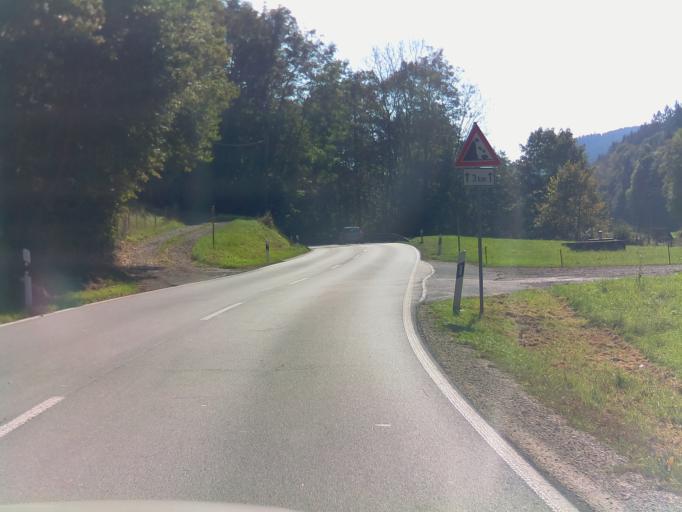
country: DE
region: Thuringia
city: Leutenberg
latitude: 50.5903
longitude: 11.4375
